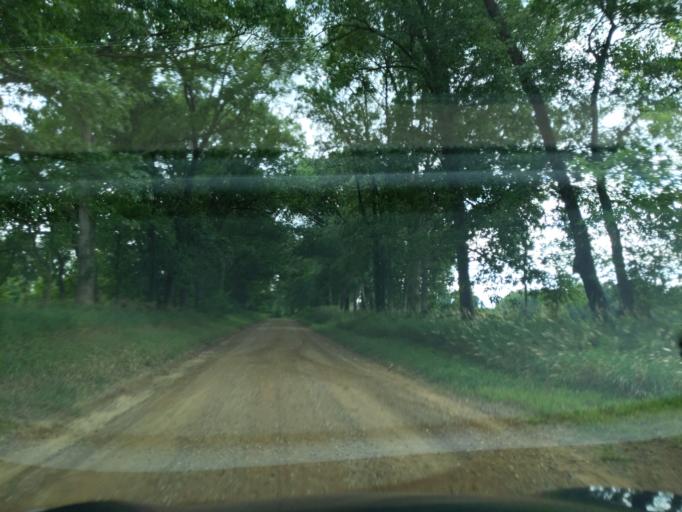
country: US
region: Michigan
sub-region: Eaton County
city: Eaton Rapids
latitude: 42.3819
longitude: -84.5808
